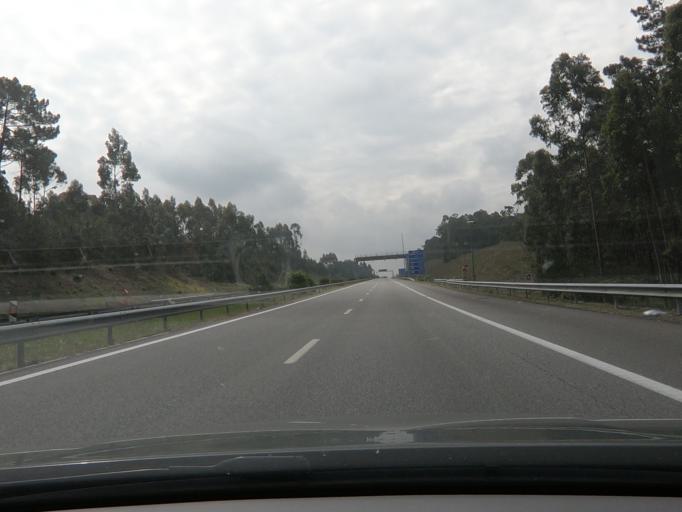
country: PT
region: Aveiro
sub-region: Aveiro
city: Oliveirinha
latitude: 40.6205
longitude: -8.5940
